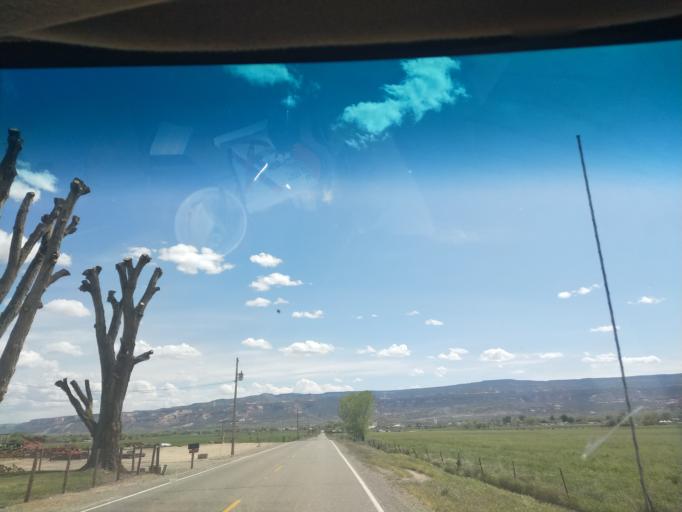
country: US
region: Colorado
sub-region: Mesa County
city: Fruita
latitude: 39.1857
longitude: -108.7571
